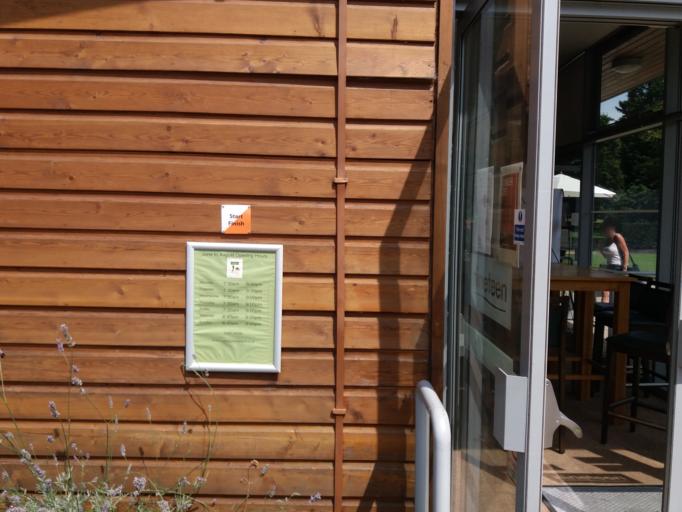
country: GB
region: England
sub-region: Lancashire
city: Chorley
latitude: 53.6310
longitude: -2.6249
